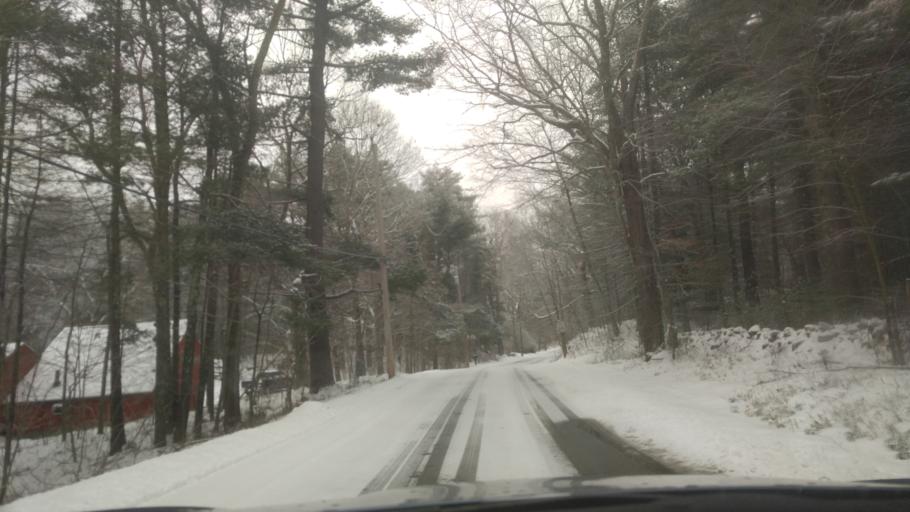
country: US
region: Rhode Island
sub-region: Providence County
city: Foster
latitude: 41.8291
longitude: -71.7505
